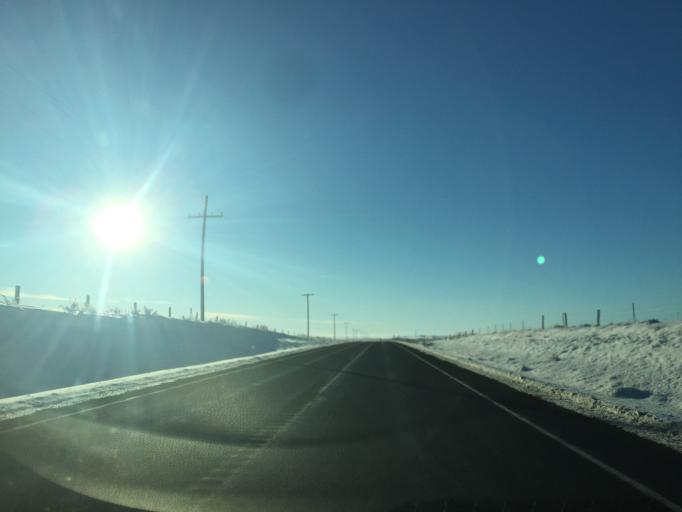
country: US
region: Washington
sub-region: Okanogan County
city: Coulee Dam
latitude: 47.7230
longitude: -118.8903
